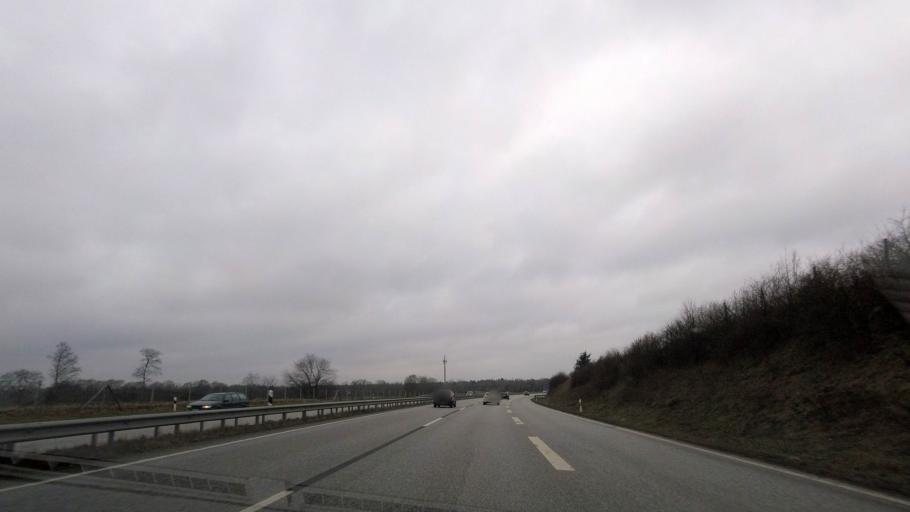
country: DE
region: Schleswig-Holstein
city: Daldorf
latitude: 54.0133
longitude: 10.2455
